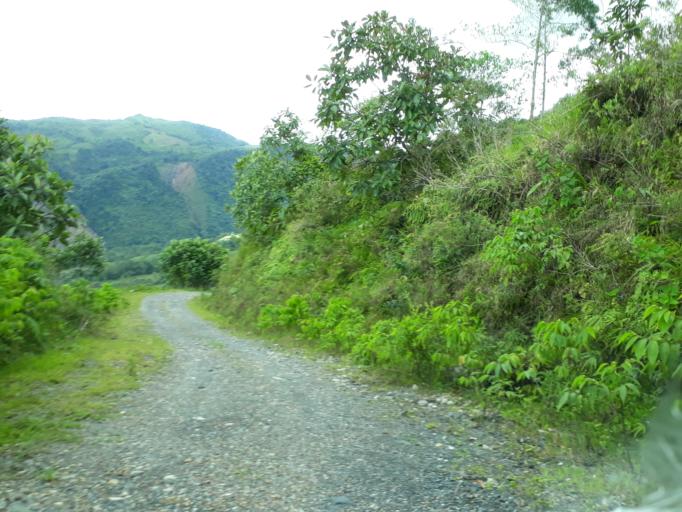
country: CO
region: Cundinamarca
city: Gachala
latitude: 4.7123
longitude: -73.3668
